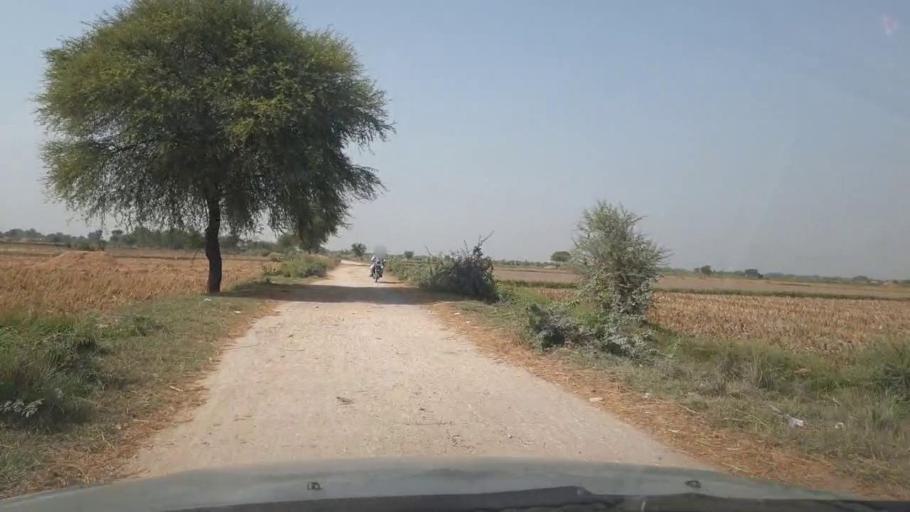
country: PK
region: Sindh
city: Bulri
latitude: 24.8706
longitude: 68.3210
